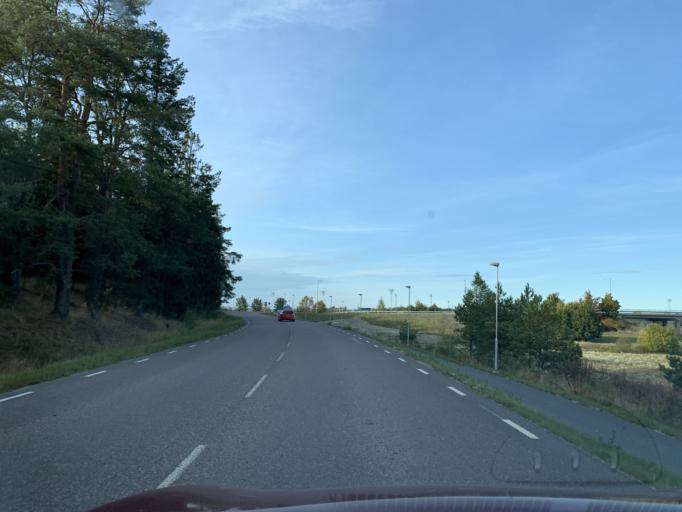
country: SE
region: Stockholm
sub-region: Upplands-Bro Kommun
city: Bro
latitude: 59.5156
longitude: 17.6149
